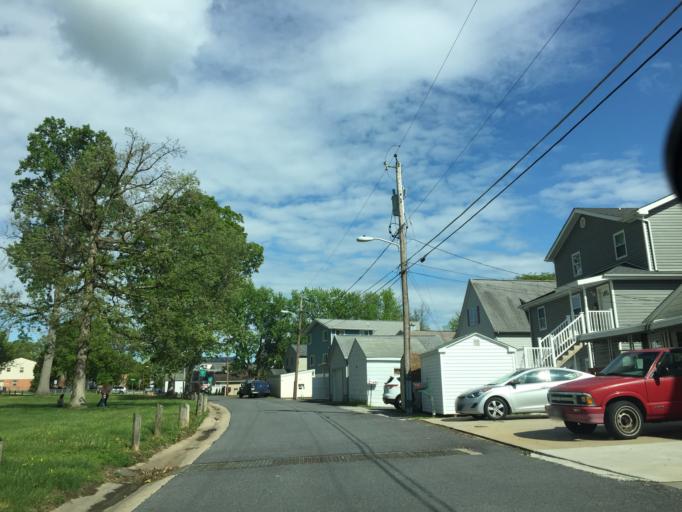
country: US
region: Maryland
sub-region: Baltimore County
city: Middle River
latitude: 39.3170
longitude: -76.4312
